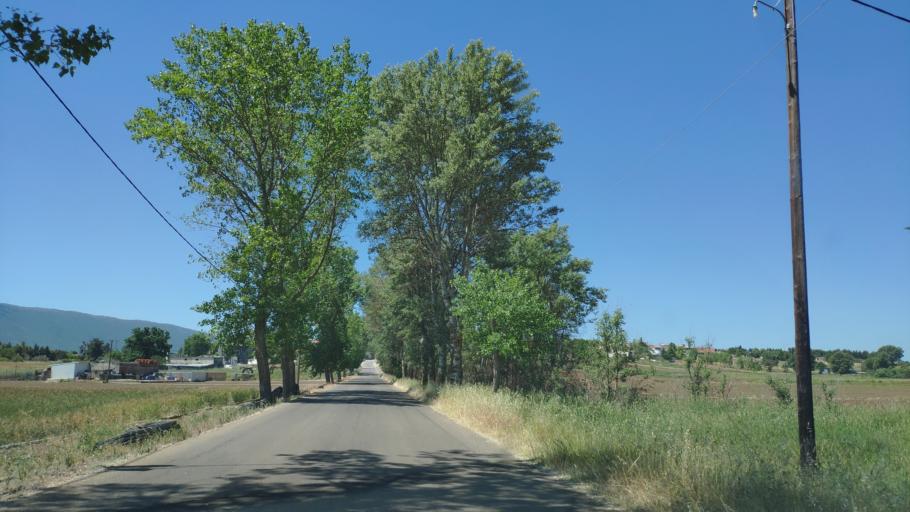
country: GR
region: Central Greece
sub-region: Nomos Voiotias
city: Kaparellion
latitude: 38.2690
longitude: 23.2433
